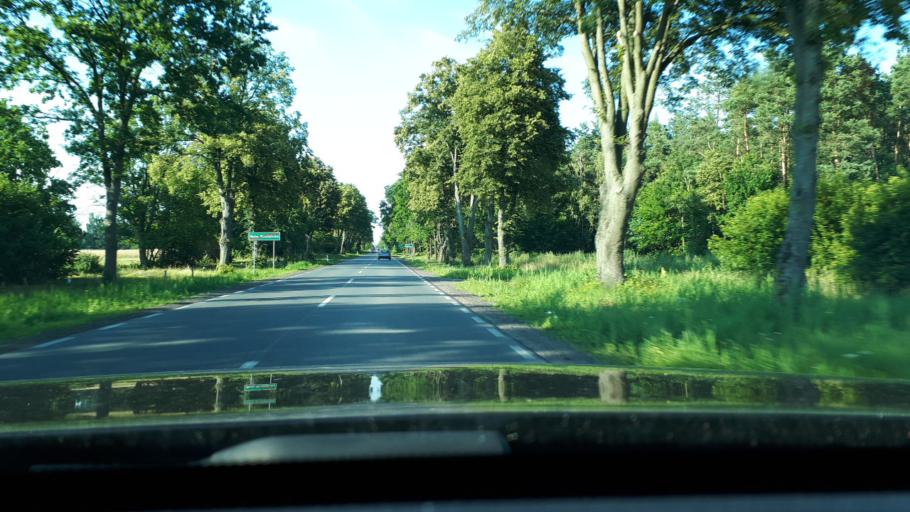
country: PL
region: Masovian Voivodeship
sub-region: Powiat ciechanowski
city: Ojrzen
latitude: 52.7380
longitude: 20.5210
